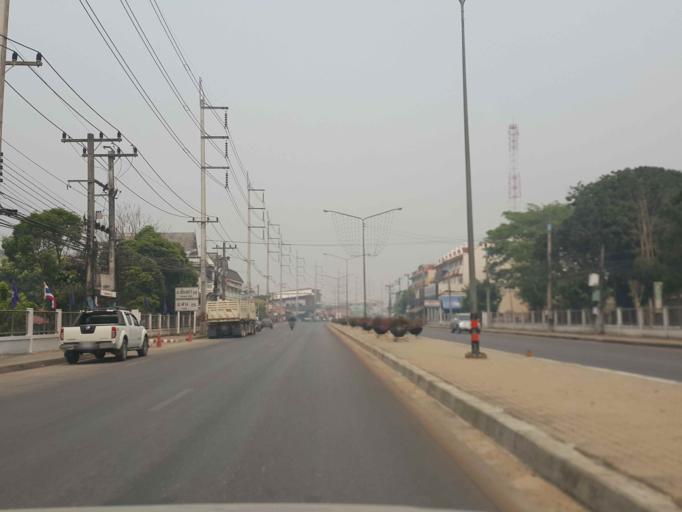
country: TH
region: Chiang Mai
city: Mae Taeng
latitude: 19.0961
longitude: 98.9360
